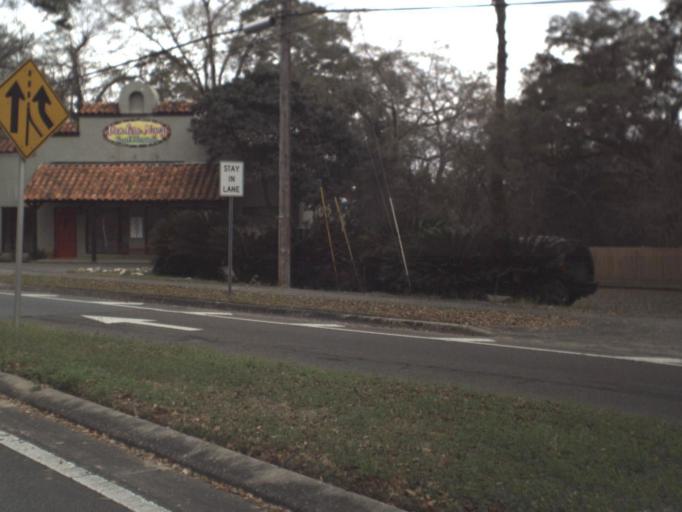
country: US
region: Florida
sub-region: Leon County
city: Tallahassee
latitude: 30.4592
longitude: -84.2757
